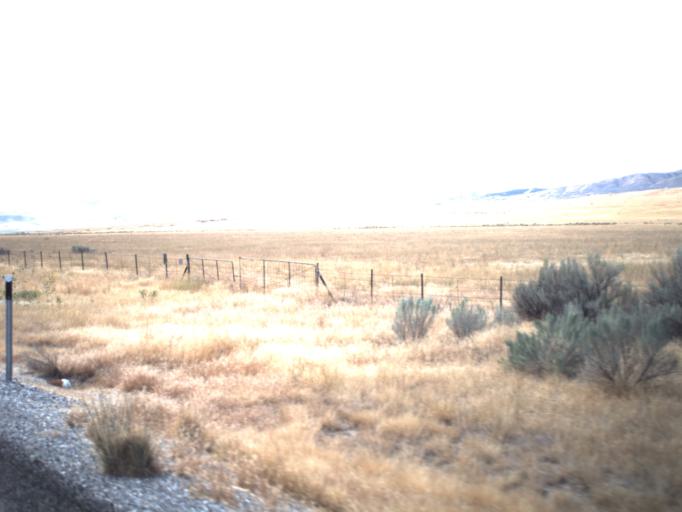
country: US
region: Utah
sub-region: Box Elder County
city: Garland
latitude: 41.8074
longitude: -112.4165
